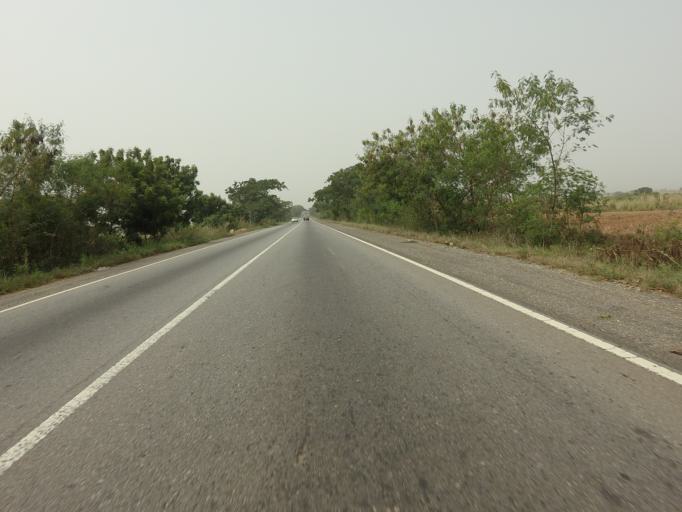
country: GH
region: Volta
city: Anloga
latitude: 5.8890
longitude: 0.4652
